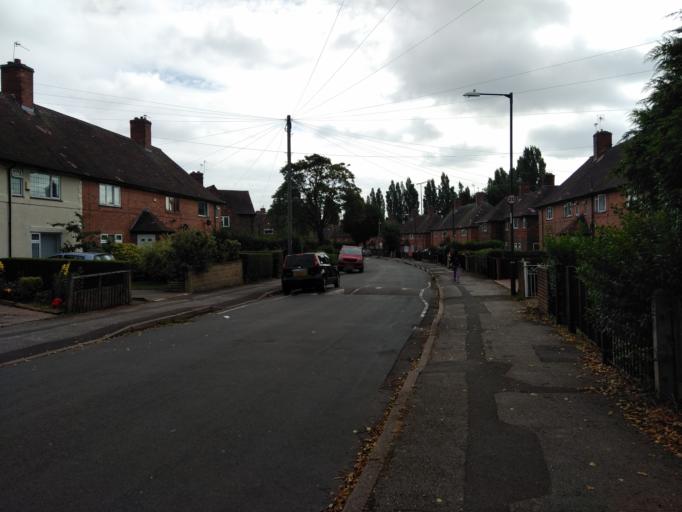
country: GB
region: England
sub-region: Nottinghamshire
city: Kimberley
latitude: 52.9693
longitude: -1.2194
